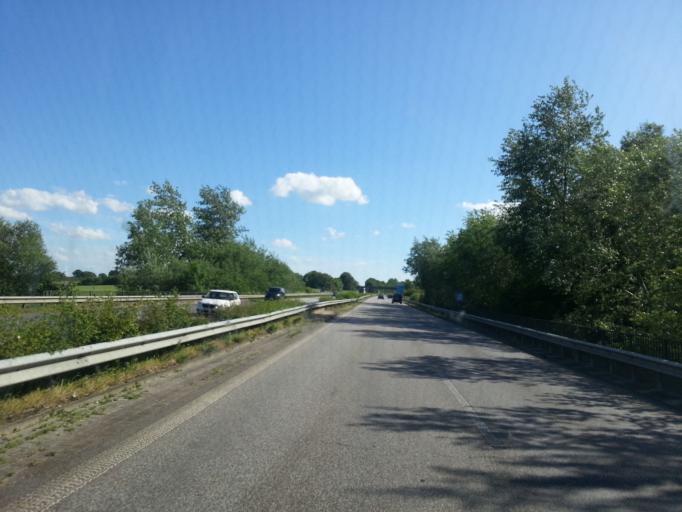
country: DE
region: Schleswig-Holstein
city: Neustadt in Holstein
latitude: 54.1054
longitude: 10.7814
